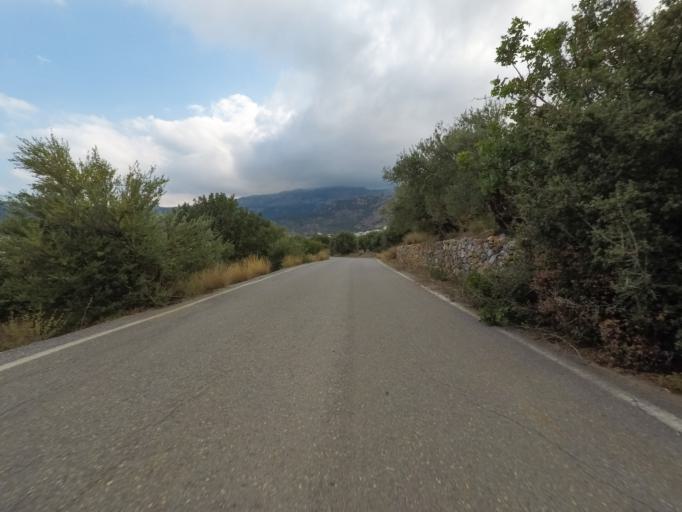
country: GR
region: Crete
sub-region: Nomos Lasithiou
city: Kritsa
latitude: 35.1640
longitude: 25.6530
